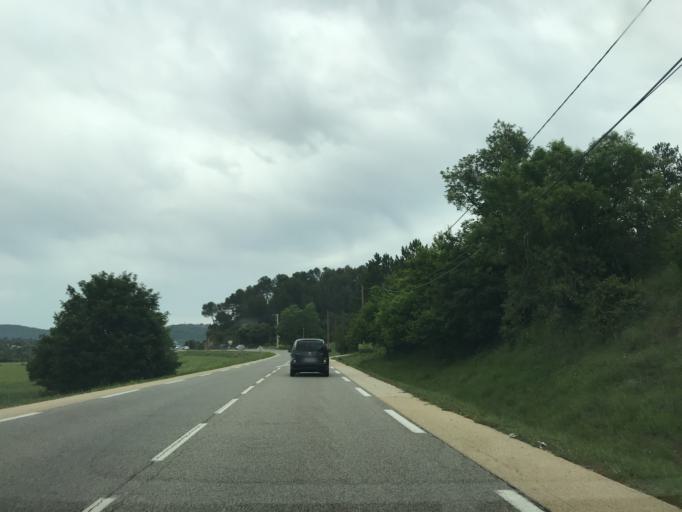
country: FR
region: Provence-Alpes-Cote d'Azur
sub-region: Departement du Var
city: Rians
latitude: 43.5978
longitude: 5.7496
